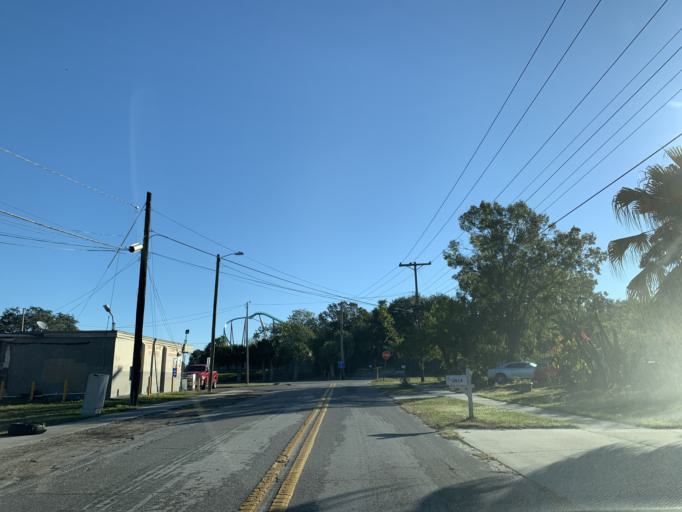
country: US
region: Florida
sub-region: Hillsborough County
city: University
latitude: 28.0399
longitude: -82.4269
